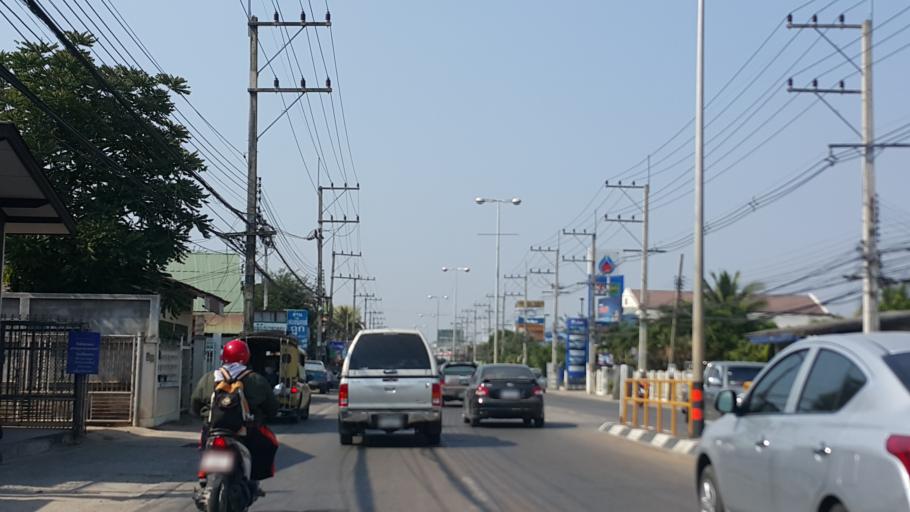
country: TH
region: Chiang Mai
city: San Sai
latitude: 18.9177
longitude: 98.9436
